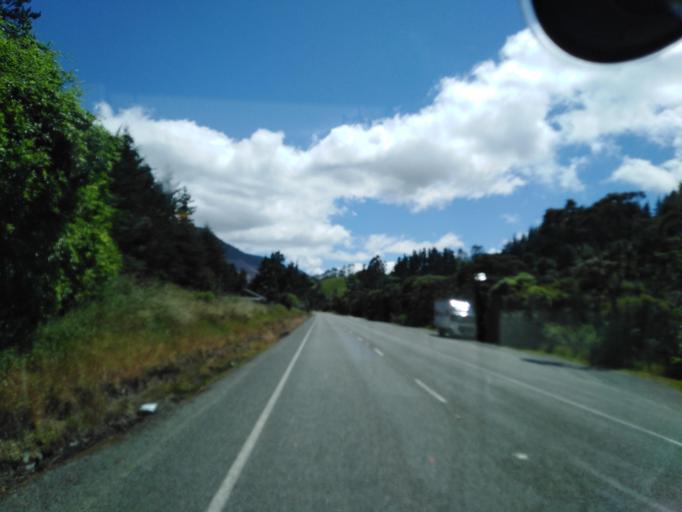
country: NZ
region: Nelson
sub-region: Nelson City
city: Nelson
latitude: -41.2234
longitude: 173.3967
